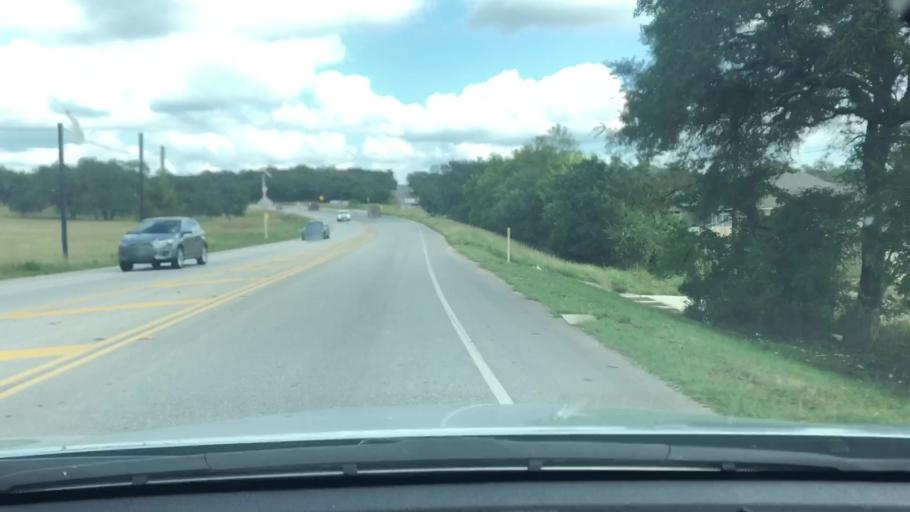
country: US
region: Texas
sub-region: Kendall County
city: Boerne
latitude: 29.7871
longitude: -98.6914
